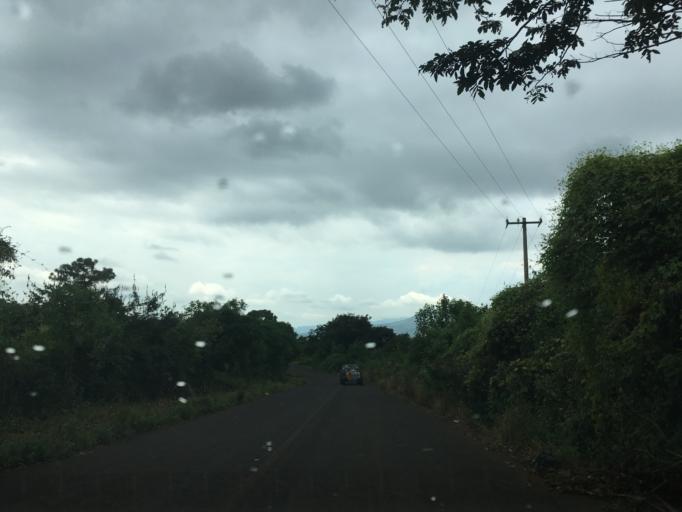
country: MX
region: Michoacan
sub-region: Periban
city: Gildardo Magana (Los Angeles)
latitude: 19.5833
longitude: -102.4358
